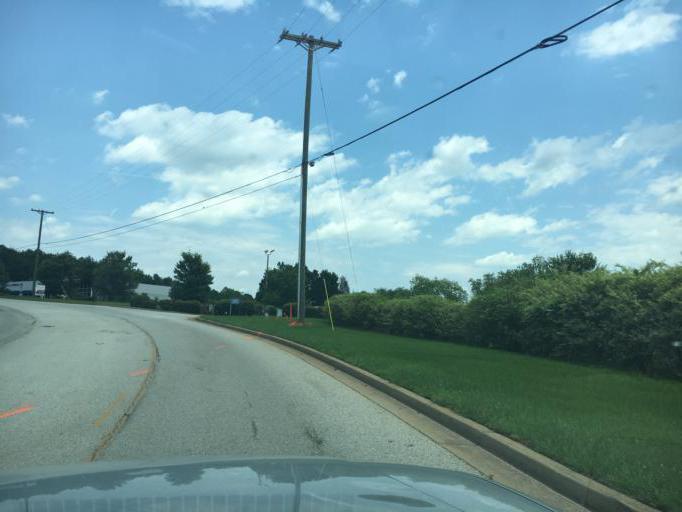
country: US
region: South Carolina
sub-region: Greenville County
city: Five Forks
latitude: 34.8714
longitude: -82.2306
